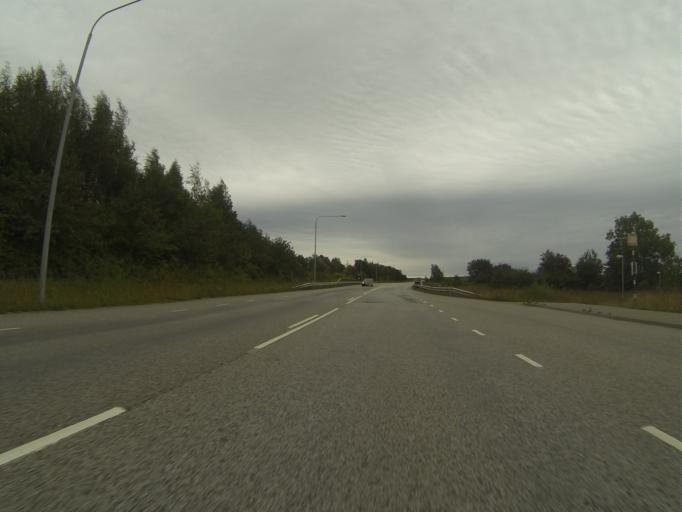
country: SE
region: Skane
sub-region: Malmo
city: Oxie
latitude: 55.5841
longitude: 13.1312
